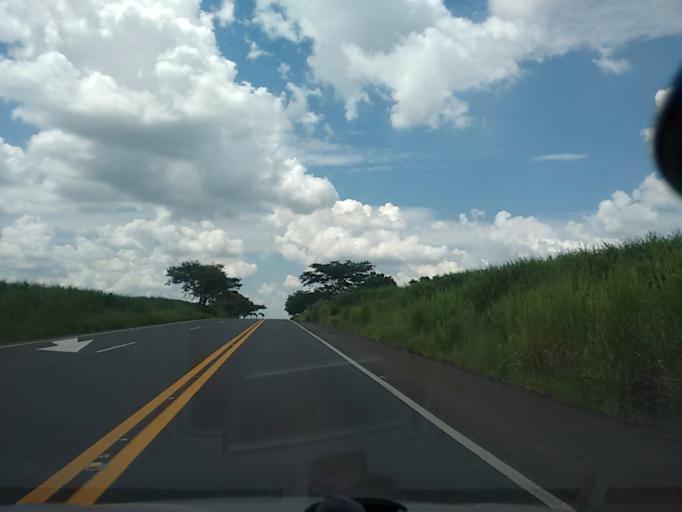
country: BR
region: Sao Paulo
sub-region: Osvaldo Cruz
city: Osvaldo Cruz
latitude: -21.8966
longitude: -50.8784
